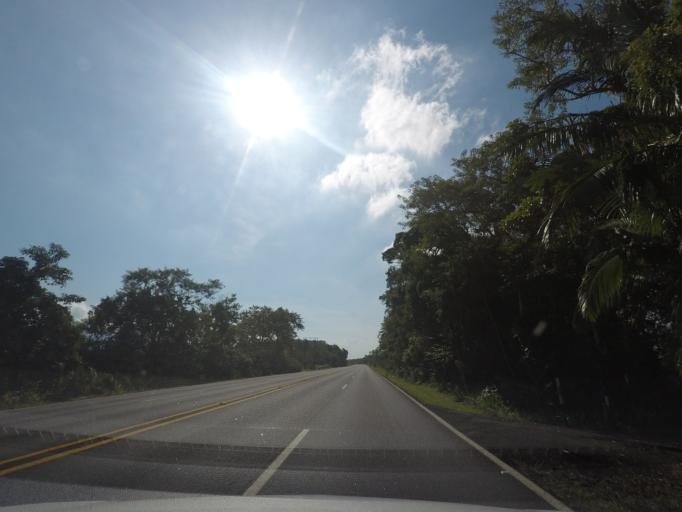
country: BR
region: Parana
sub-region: Pontal Do Parana
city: Pontal do Parana
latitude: -25.6340
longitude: -48.5939
